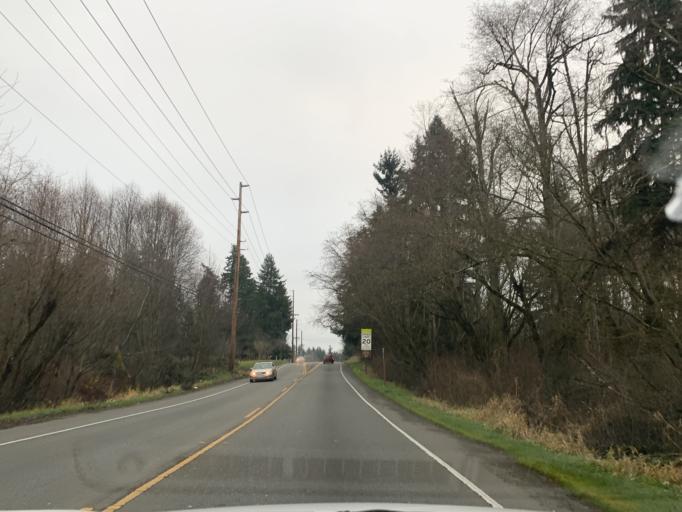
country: US
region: Washington
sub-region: Pierce County
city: Fife Heights
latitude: 47.2826
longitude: -122.3276
